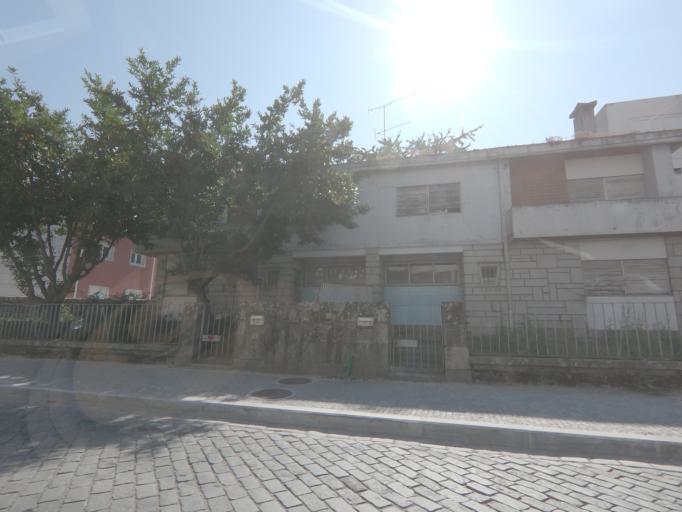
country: PT
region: Viseu
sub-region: Moimenta da Beira
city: Moimenta da Beira
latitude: 40.9789
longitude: -7.6129
